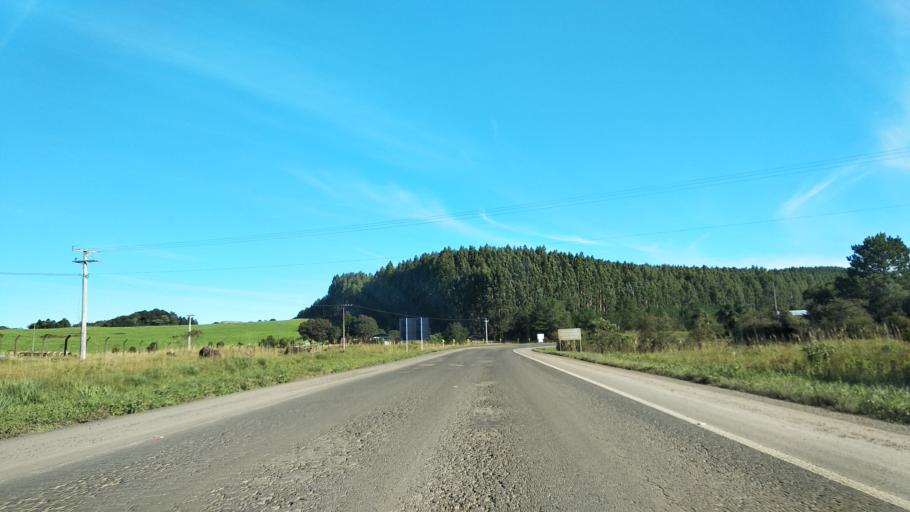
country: BR
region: Santa Catarina
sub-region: Campos Novos
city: Campos Novos
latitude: -27.3975
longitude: -51.1942
